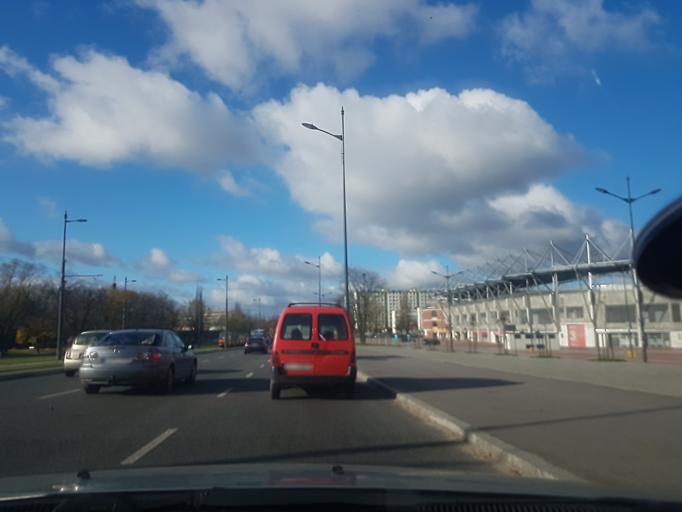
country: PL
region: Lodz Voivodeship
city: Lodz
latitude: 51.7640
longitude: 19.5144
